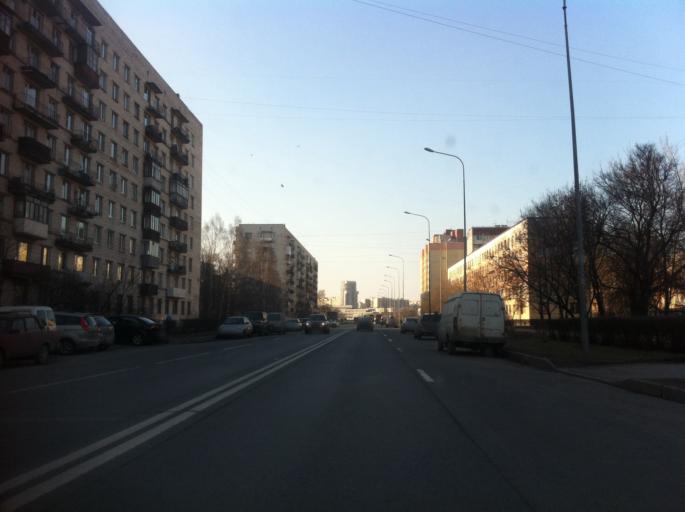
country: RU
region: St.-Petersburg
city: Dachnoye
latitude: 59.8449
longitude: 30.2320
